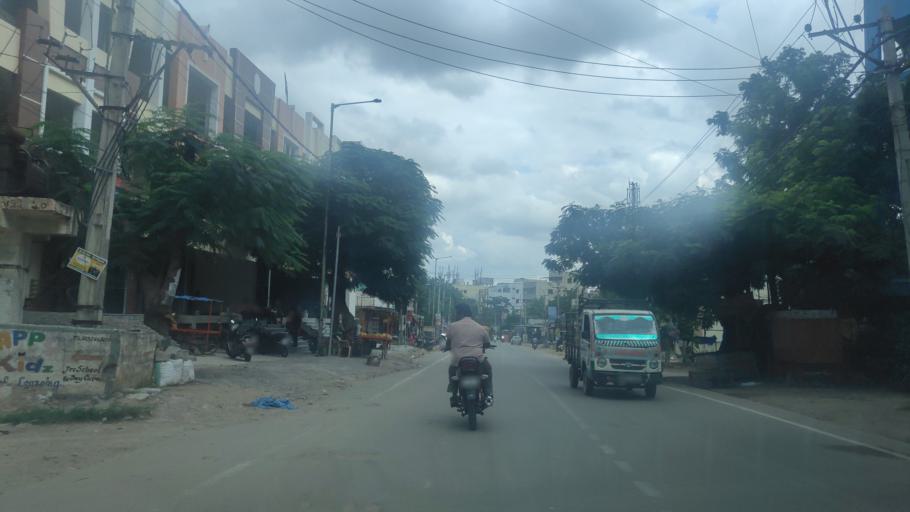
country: IN
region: Telangana
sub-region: Medak
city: Serilingampalle
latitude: 17.5068
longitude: 78.3546
